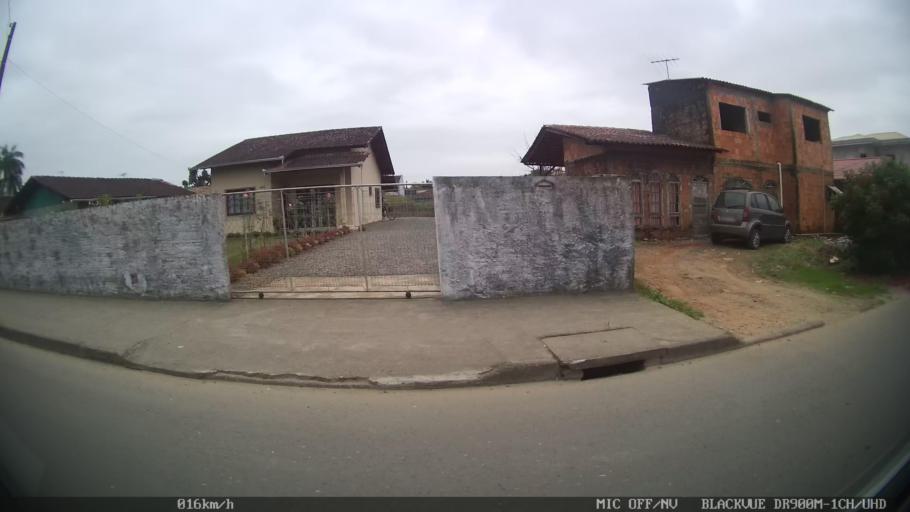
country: BR
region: Santa Catarina
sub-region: Joinville
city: Joinville
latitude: -26.3560
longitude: -48.8280
